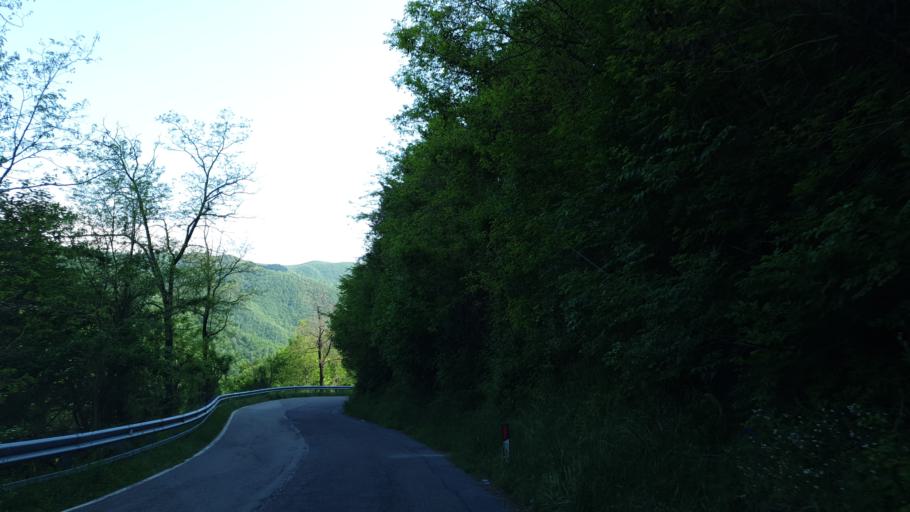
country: IT
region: Tuscany
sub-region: Province of Arezzo
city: Soci
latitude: 43.7854
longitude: 11.8688
